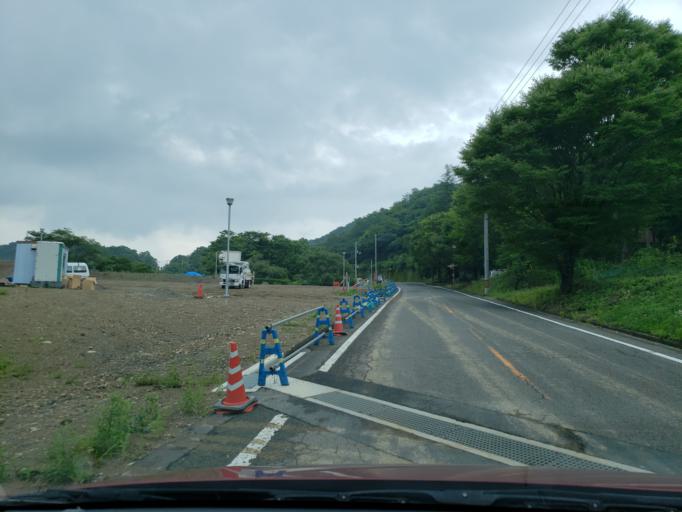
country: JP
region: Tokushima
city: Kamojimacho-jogejima
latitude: 34.1128
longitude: 134.2976
